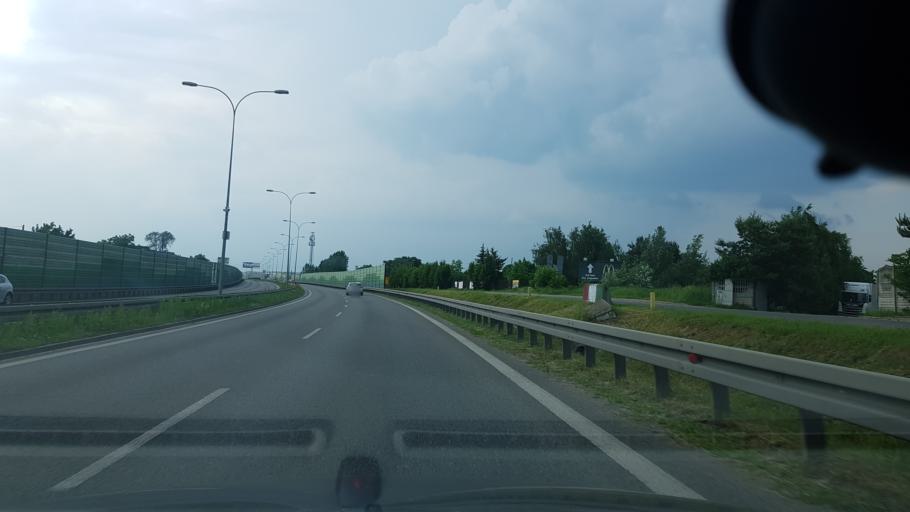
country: PL
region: Masovian Voivodeship
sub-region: Powiat legionowski
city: Jablonna
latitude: 52.3680
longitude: 20.9353
